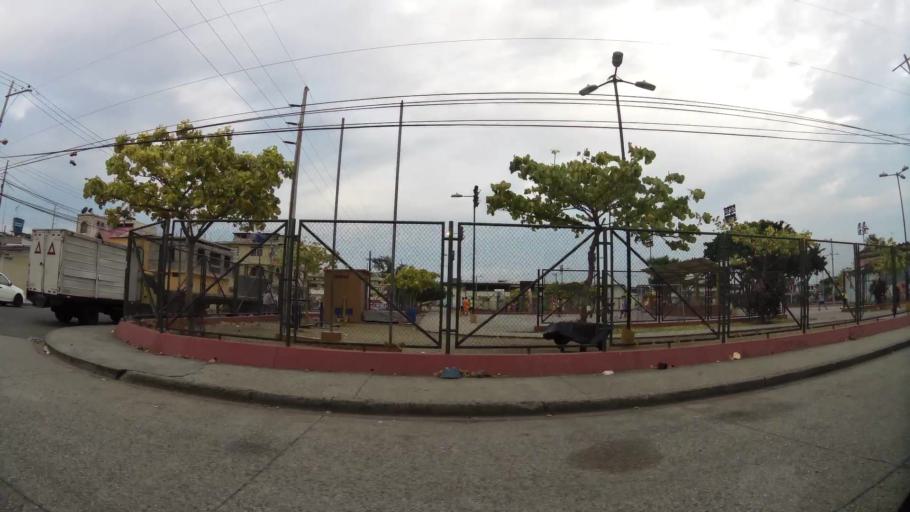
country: EC
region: Guayas
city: Guayaquil
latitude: -2.2383
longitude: -79.8889
